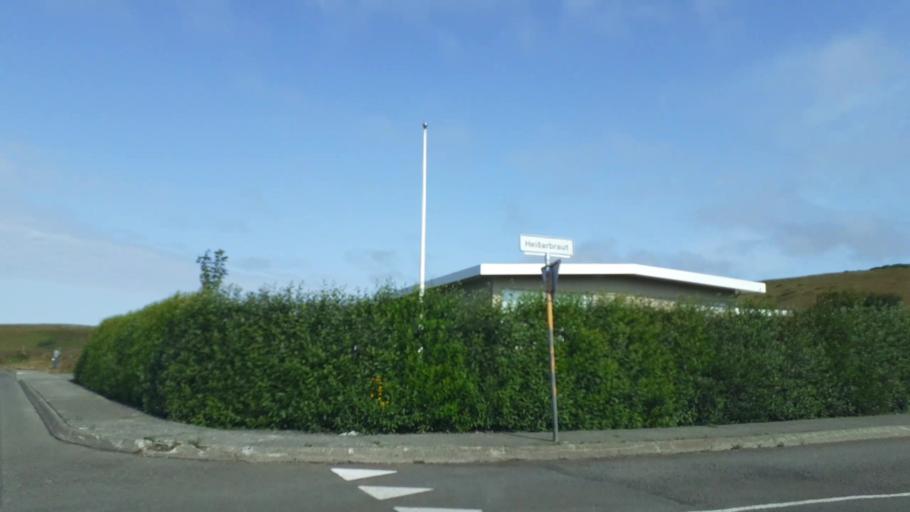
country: IS
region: Northwest
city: Saudarkrokur
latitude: 65.6627
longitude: -20.2803
